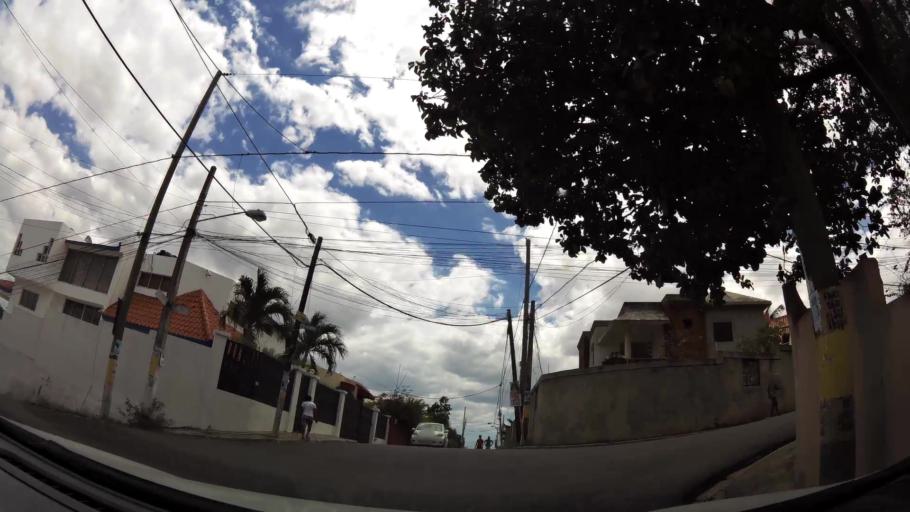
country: DO
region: Nacional
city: Ensanche Luperon
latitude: 18.5241
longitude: -69.9082
